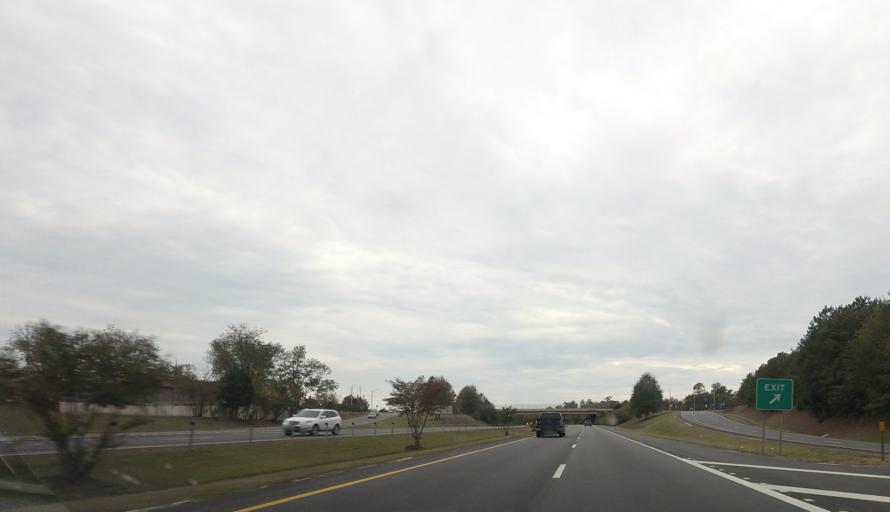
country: US
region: Alabama
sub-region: Russell County
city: Phenix City
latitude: 32.5003
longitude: -85.0150
